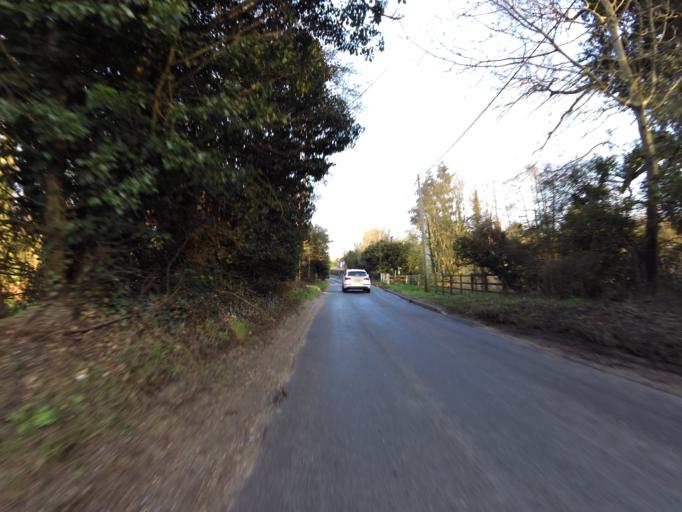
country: GB
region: England
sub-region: Suffolk
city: Woodbridge
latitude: 52.0784
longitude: 1.2811
